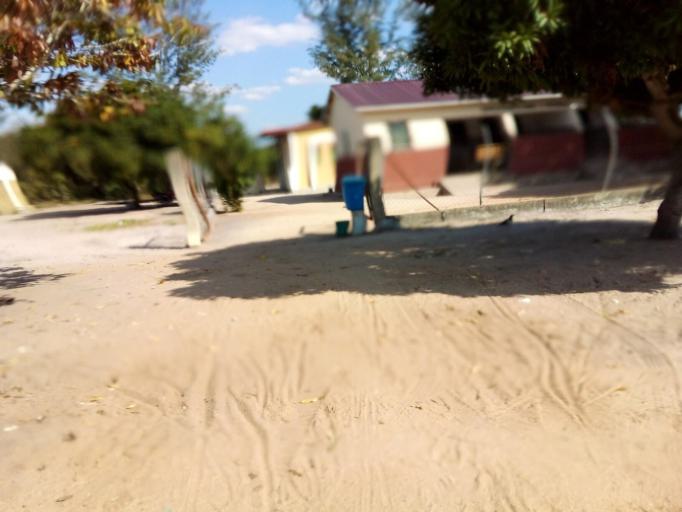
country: MZ
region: Zambezia
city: Quelimane
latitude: -17.5746
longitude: 36.6145
